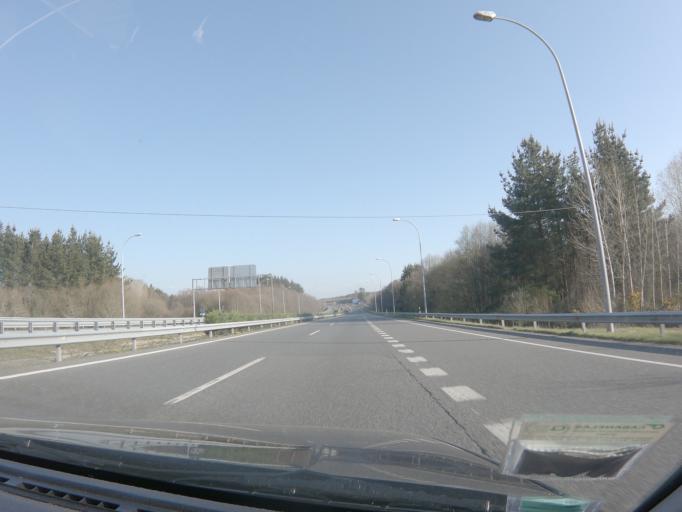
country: ES
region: Galicia
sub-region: Provincia de Lugo
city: Lugo
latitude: 43.0551
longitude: -7.5555
